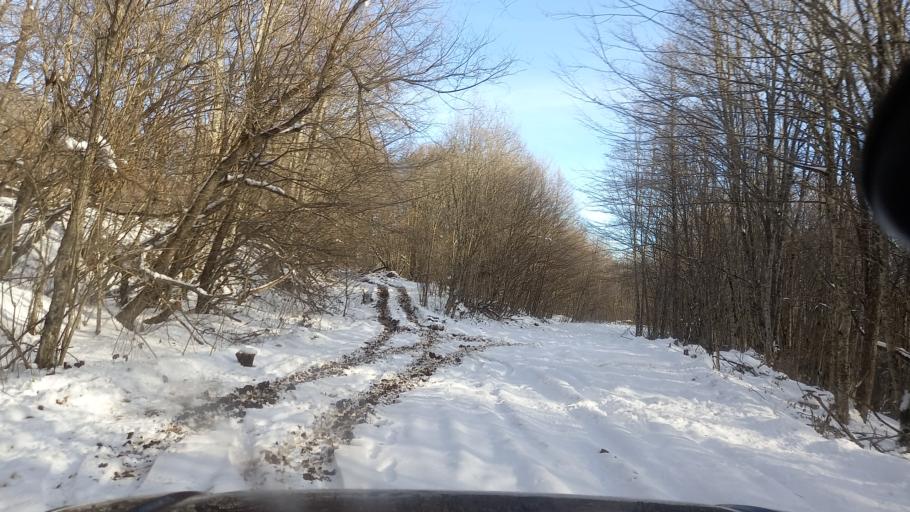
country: RU
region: Adygeya
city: Kamennomostskiy
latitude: 44.2280
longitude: 40.0946
